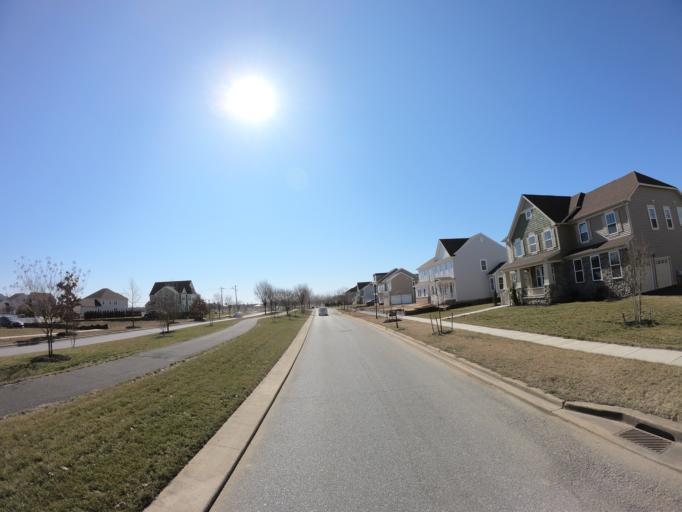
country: US
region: Delaware
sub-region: New Castle County
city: Middletown
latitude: 39.5072
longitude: -75.6667
